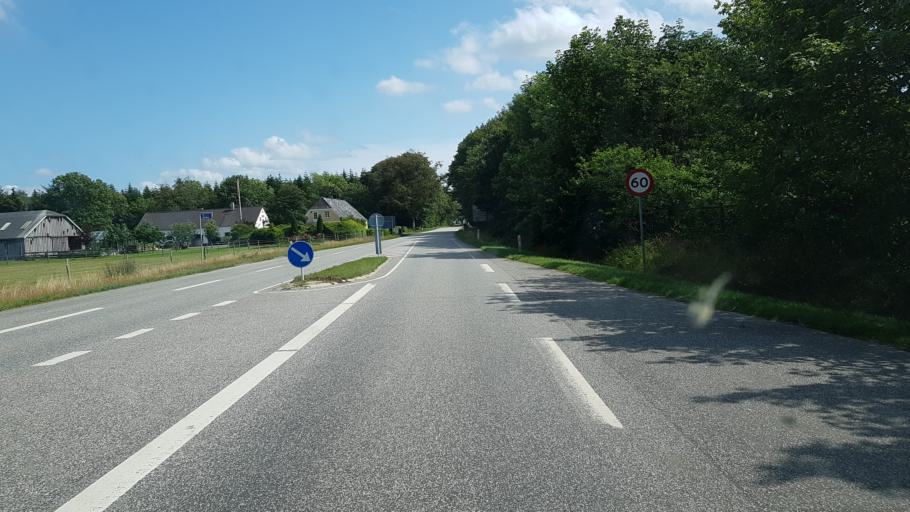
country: DK
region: South Denmark
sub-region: Billund Kommune
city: Billund
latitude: 55.6674
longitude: 9.1969
